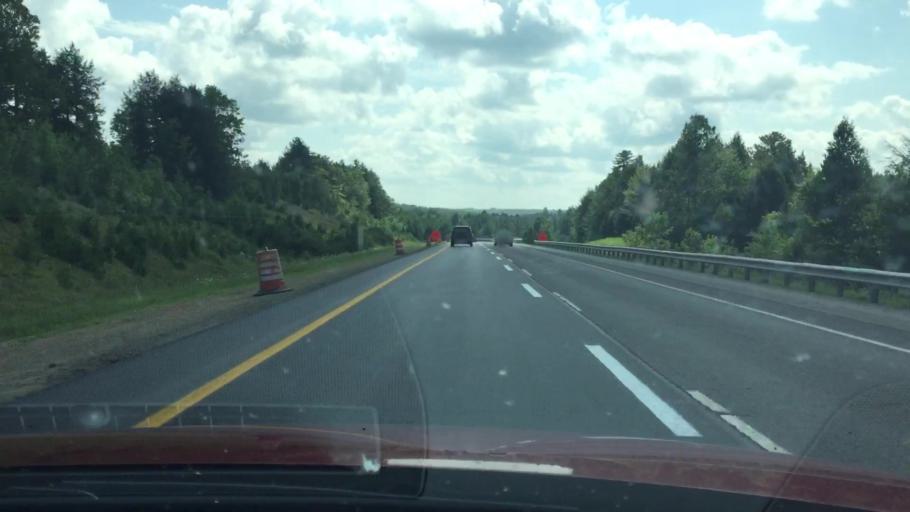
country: US
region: Maine
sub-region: Penobscot County
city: Medway
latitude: 45.6468
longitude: -68.4995
